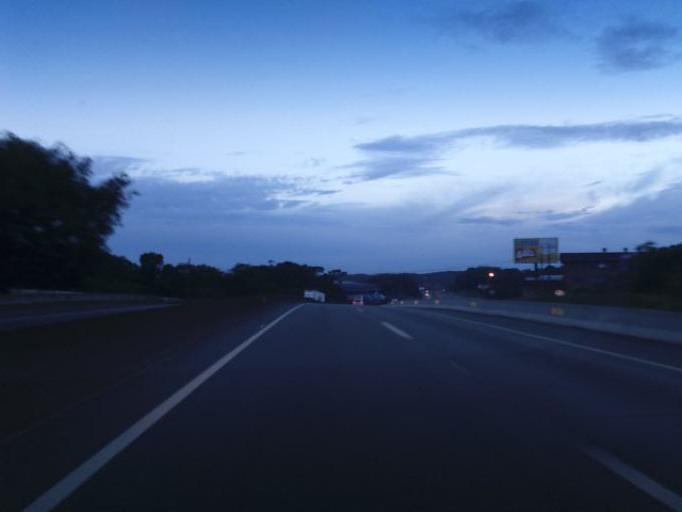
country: BR
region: Santa Catarina
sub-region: Joinville
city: Joinville
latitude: -26.3357
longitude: -48.8599
